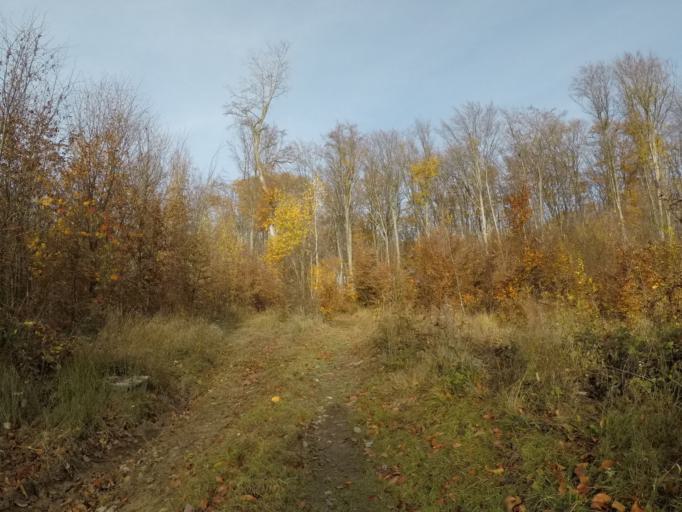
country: SK
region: Presovsky
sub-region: Okres Presov
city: Presov
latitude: 48.9088
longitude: 21.2157
